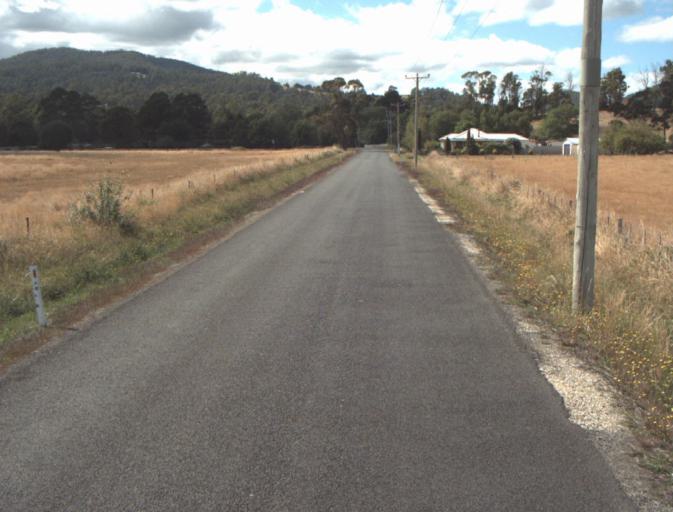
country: AU
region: Tasmania
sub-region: Launceston
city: Mayfield
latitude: -41.2596
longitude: 147.1557
